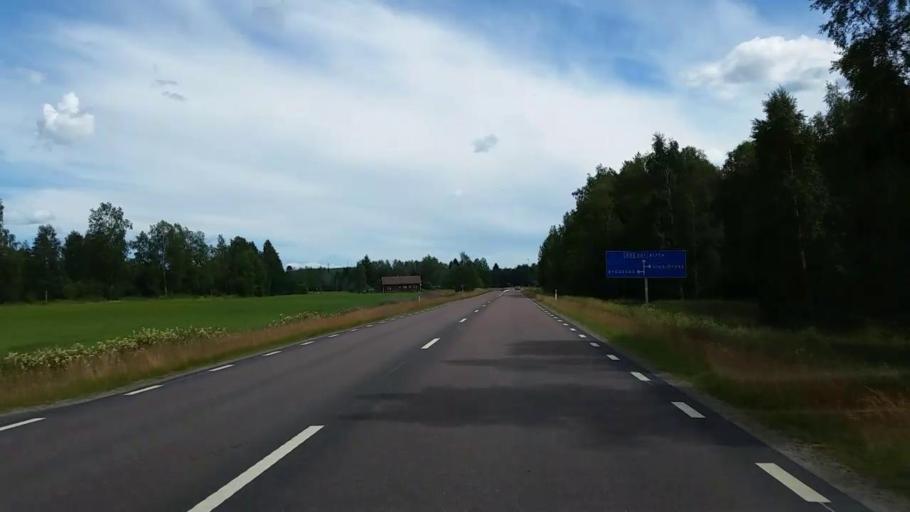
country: SE
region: Gaevleborg
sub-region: Ovanakers Kommun
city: Edsbyn
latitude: 61.3646
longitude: 15.8860
